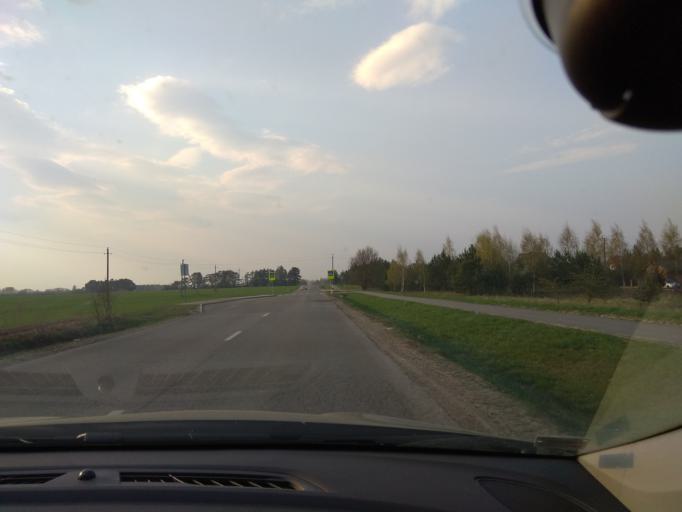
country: LT
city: Grigiskes
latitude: 54.6166
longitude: 25.1172
